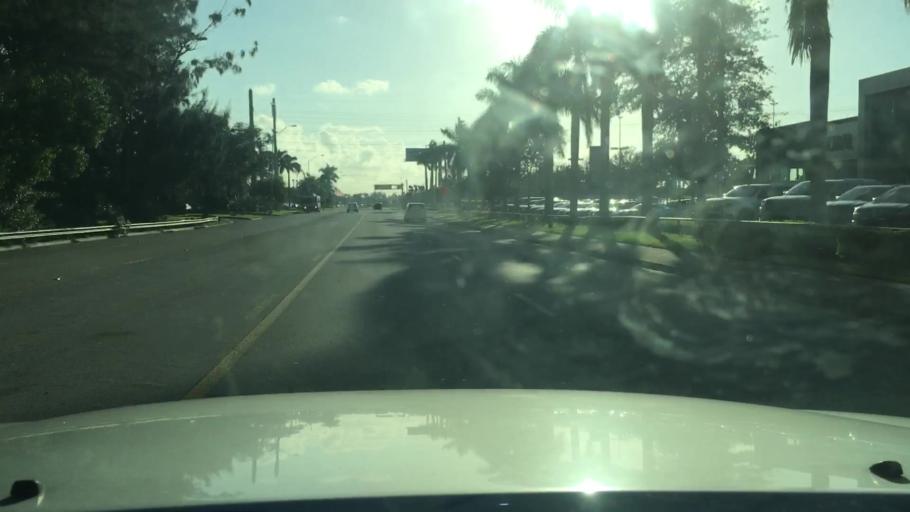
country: US
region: Florida
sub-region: Miami-Dade County
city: Fountainebleau
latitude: 25.7832
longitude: -80.3430
